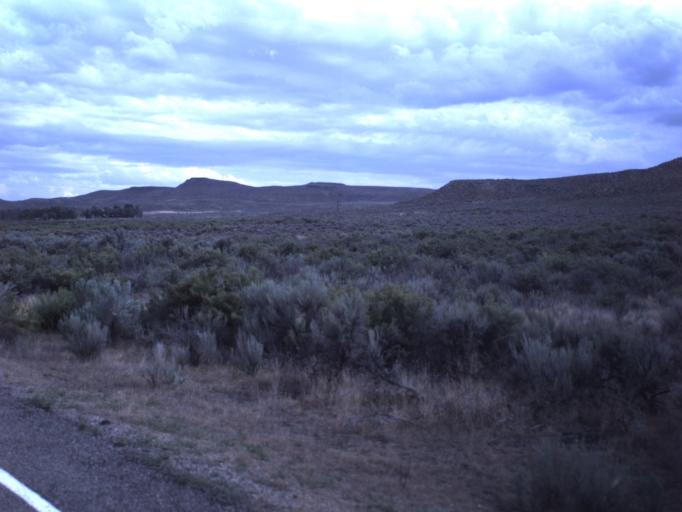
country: US
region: Colorado
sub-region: Rio Blanco County
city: Rangely
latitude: 40.0307
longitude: -109.1800
